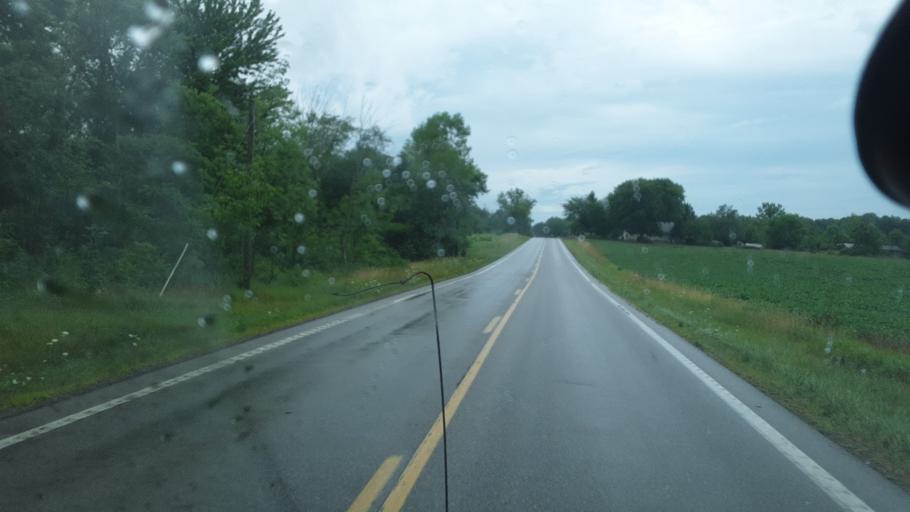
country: US
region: Indiana
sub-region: Steuben County
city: Hamilton
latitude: 41.6325
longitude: -84.7952
